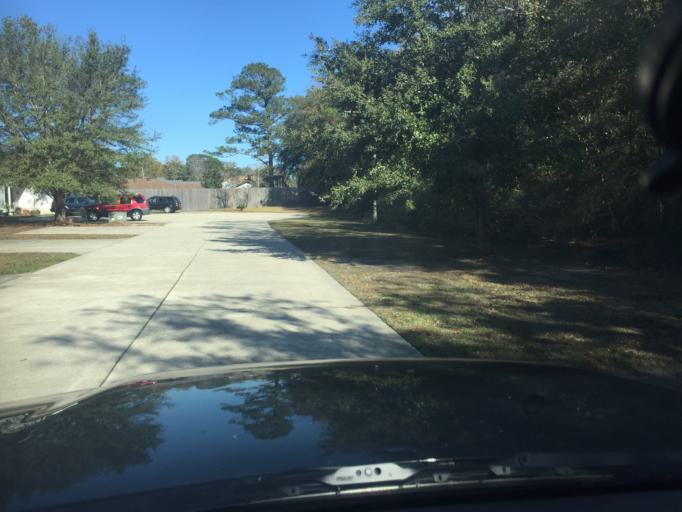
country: US
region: Louisiana
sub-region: Saint Tammany Parish
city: Slidell
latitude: 30.3089
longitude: -89.7336
